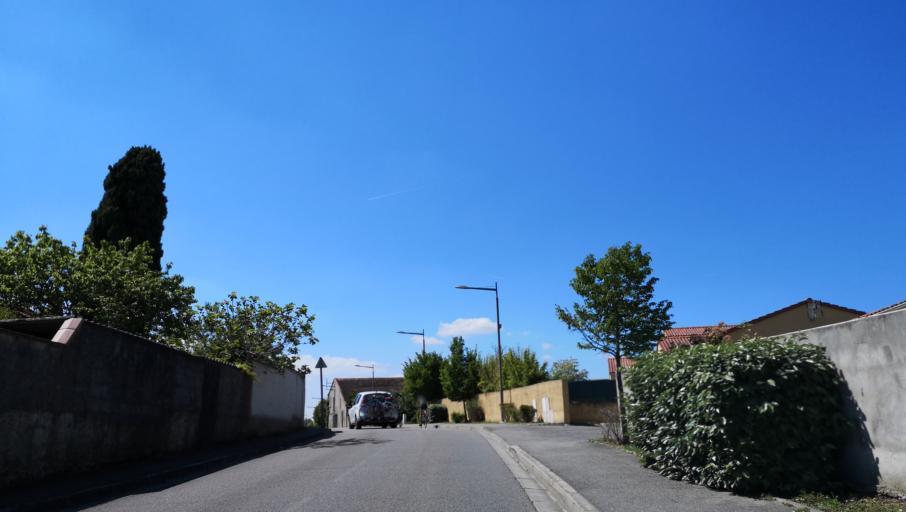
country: FR
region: Midi-Pyrenees
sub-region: Departement de la Haute-Garonne
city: Beauzelle
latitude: 43.6671
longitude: 1.3829
